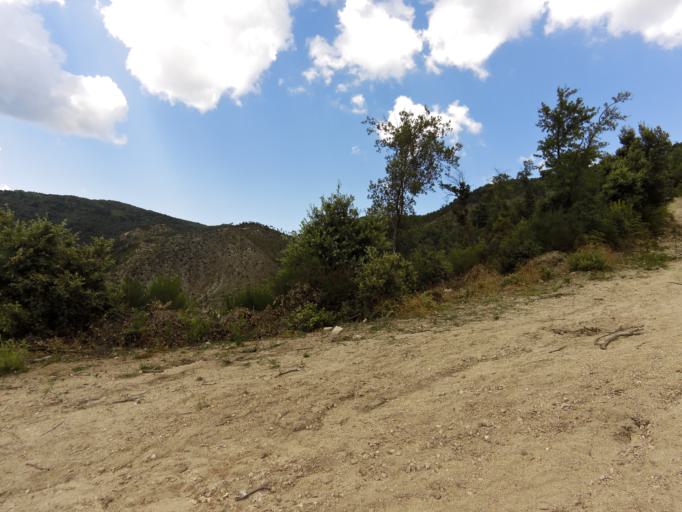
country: IT
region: Calabria
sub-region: Provincia di Reggio Calabria
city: Bivongi
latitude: 38.5057
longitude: 16.3979
